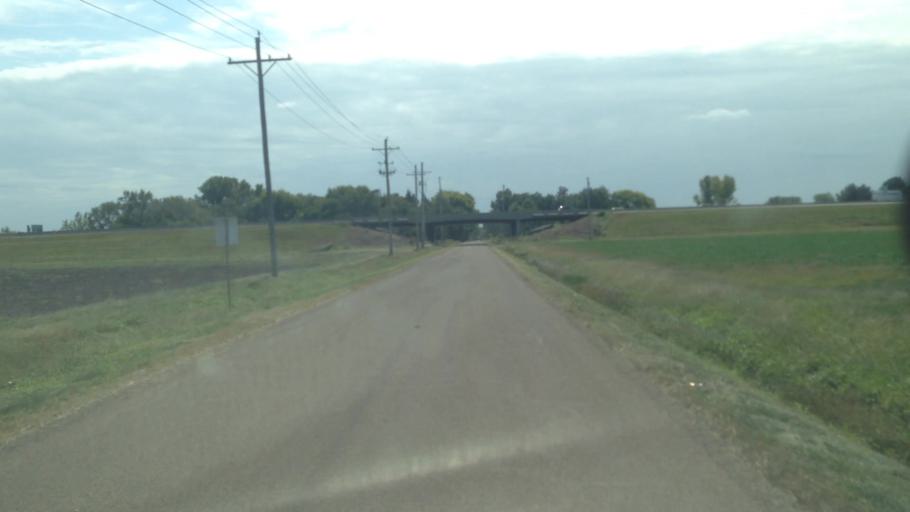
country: US
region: Kansas
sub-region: Douglas County
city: Lawrence
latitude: 38.9959
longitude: -95.2241
